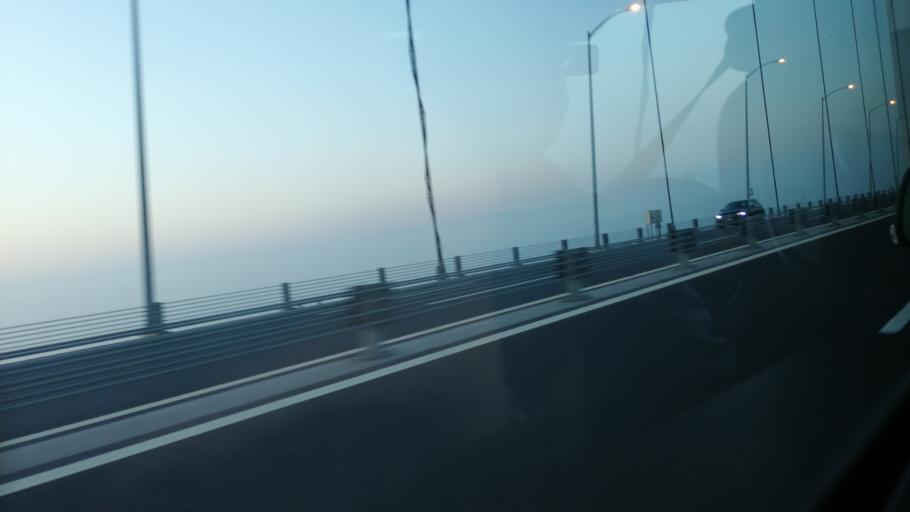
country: TR
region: Kocaeli
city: Tavsancil
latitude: 40.7599
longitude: 29.5167
